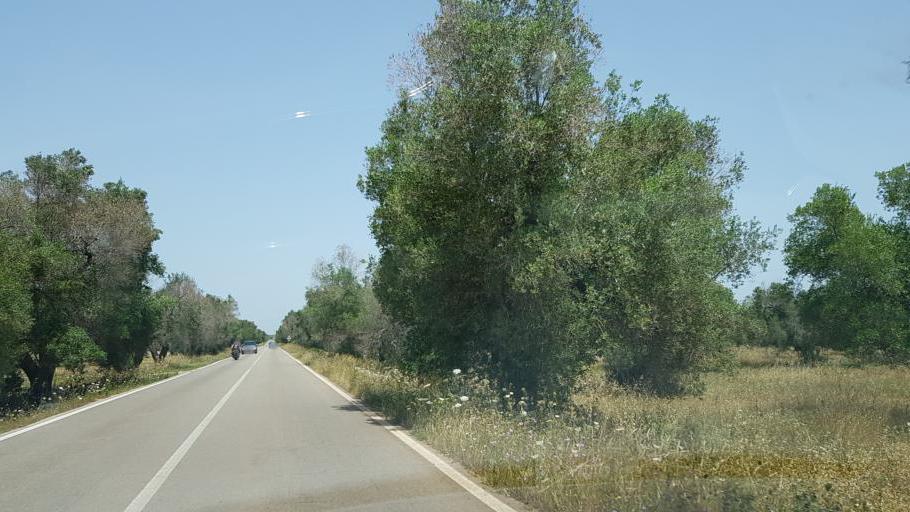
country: IT
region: Apulia
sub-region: Provincia di Lecce
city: Veglie
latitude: 40.3174
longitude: 17.9227
